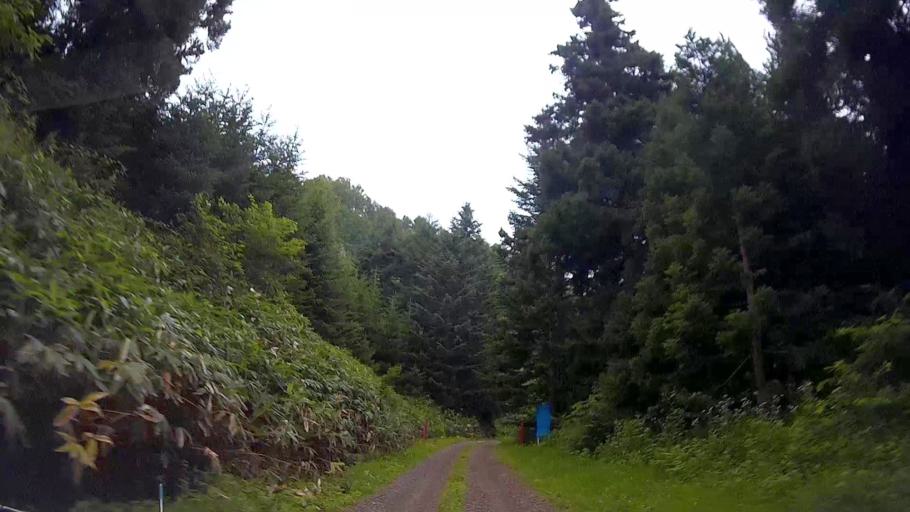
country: JP
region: Hokkaido
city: Nanae
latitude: 42.1259
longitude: 140.4271
